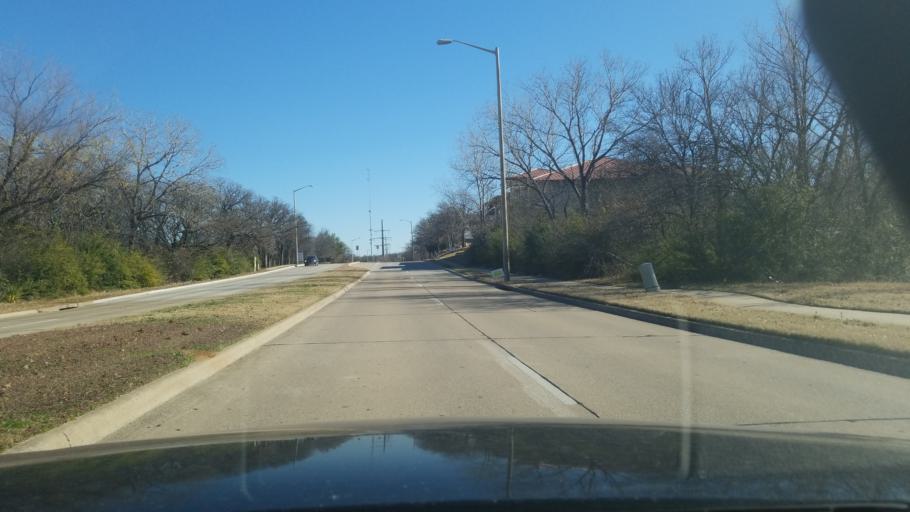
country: US
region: Texas
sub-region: Denton County
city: Corinth
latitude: 33.1821
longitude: -97.0975
